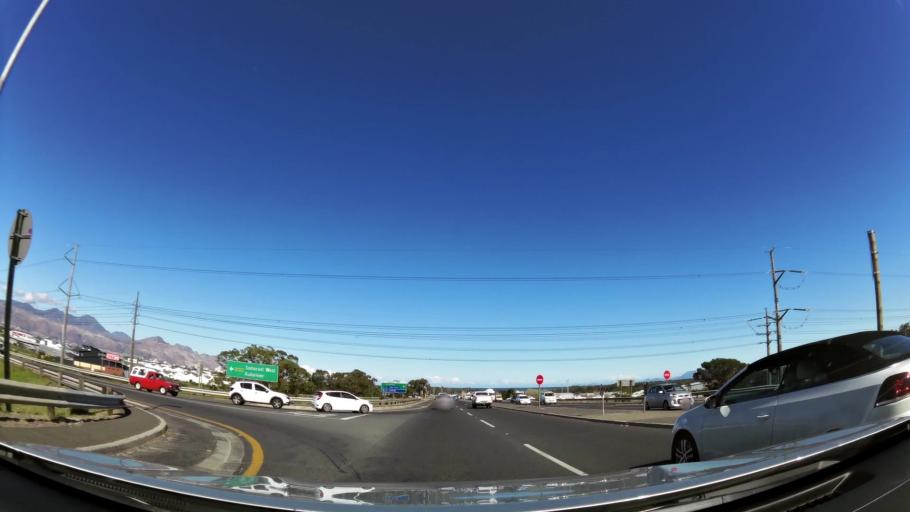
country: ZA
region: Western Cape
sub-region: Cape Winelands District Municipality
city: Stellenbosch
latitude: -34.0752
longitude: 18.8221
